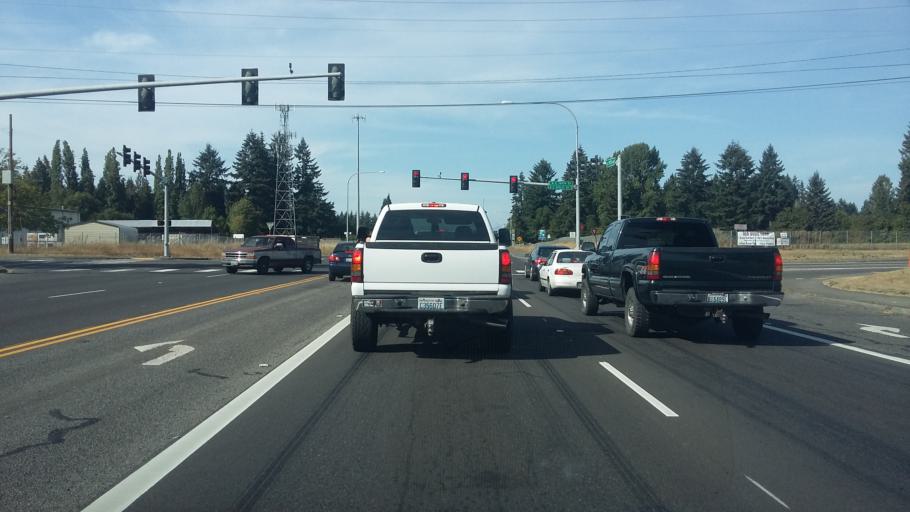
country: US
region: Washington
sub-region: Clark County
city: Brush Prairie
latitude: 45.7293
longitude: -122.5524
